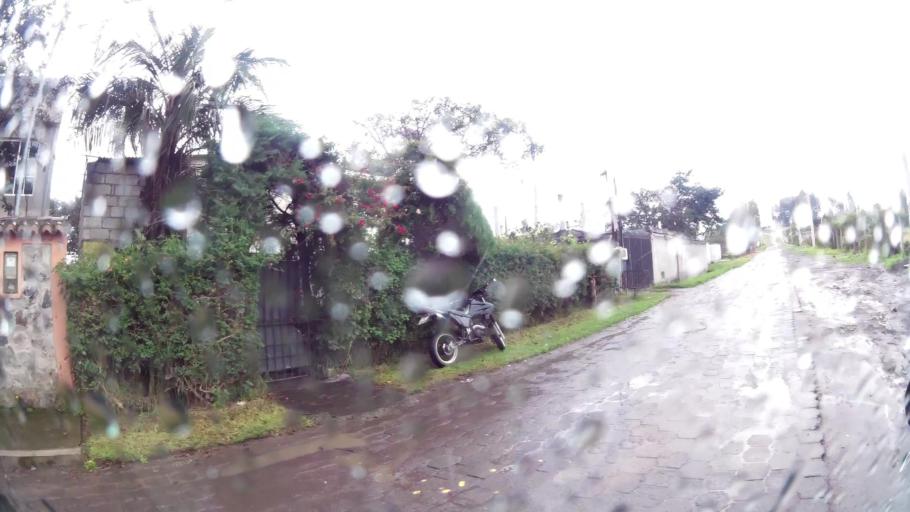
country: EC
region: Pichincha
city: Sangolqui
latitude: -0.3005
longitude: -78.4425
